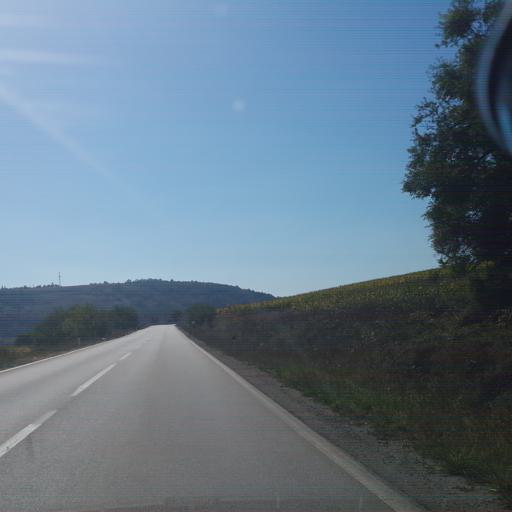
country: RS
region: Central Serbia
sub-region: Nisavski Okrug
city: Svrljig
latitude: 43.4545
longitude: 22.2021
